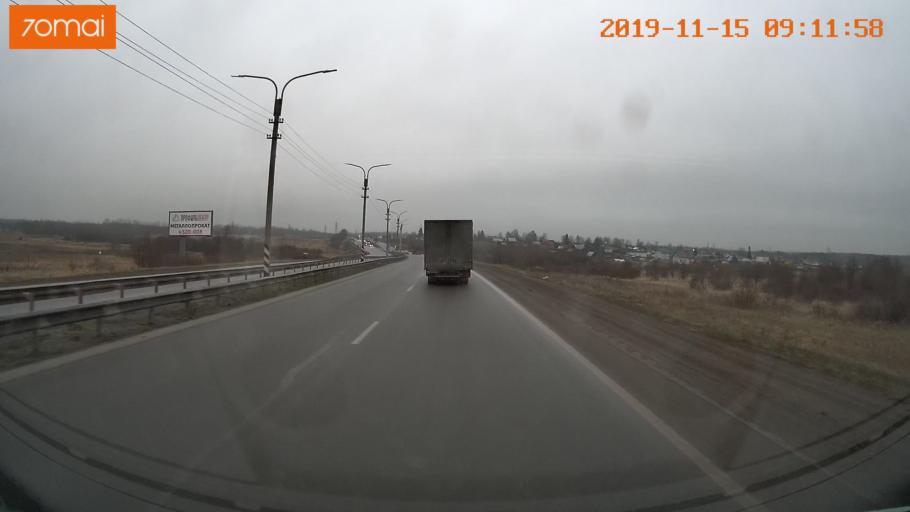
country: RU
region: Vologda
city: Tonshalovo
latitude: 59.2032
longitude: 37.9419
